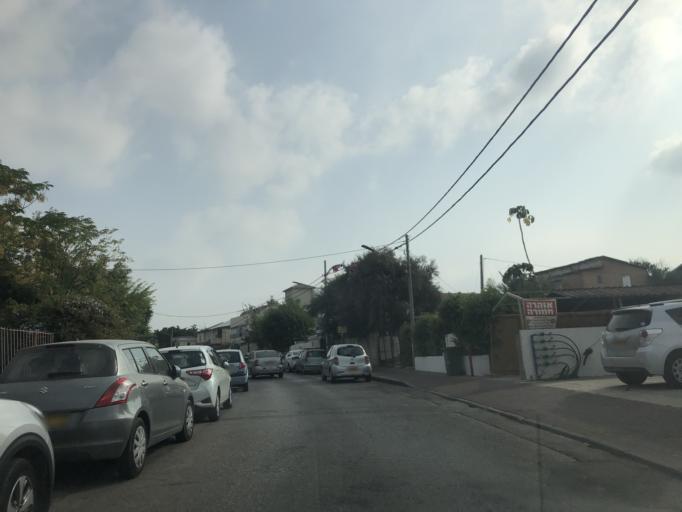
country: IL
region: Central District
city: Rosh Ha'Ayin
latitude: 32.0960
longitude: 34.9505
